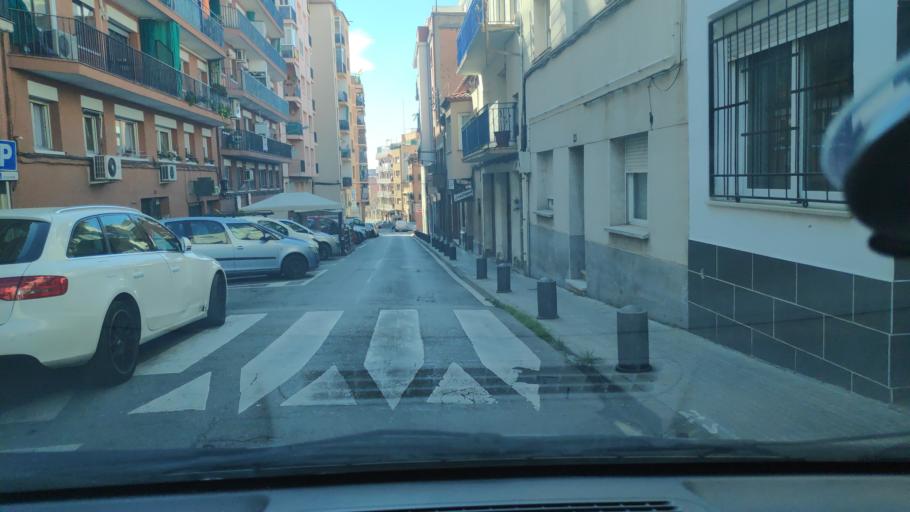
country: ES
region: Catalonia
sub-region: Provincia de Barcelona
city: Rubi
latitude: 41.4971
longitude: 2.0410
